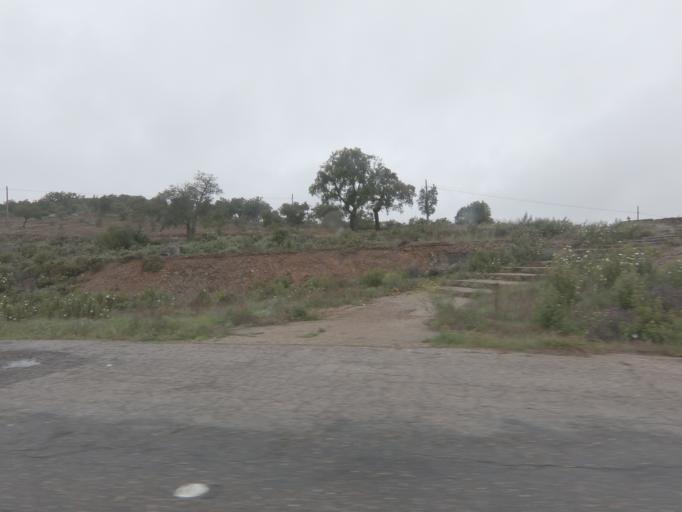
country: ES
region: Extremadura
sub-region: Provincia de Badajoz
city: Puebla de Obando
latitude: 39.1654
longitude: -6.6346
